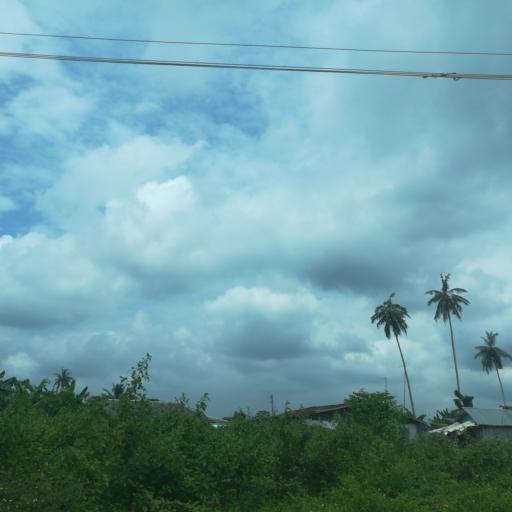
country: NG
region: Lagos
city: Ejirin
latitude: 6.6237
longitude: 3.7055
